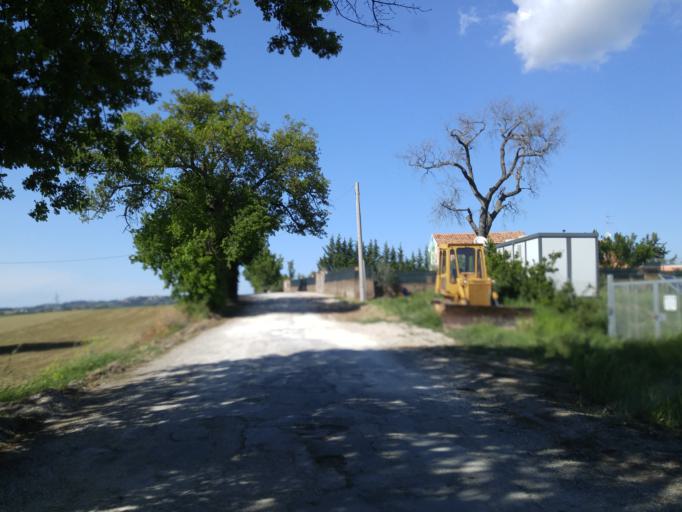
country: IT
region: The Marches
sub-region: Provincia di Pesaro e Urbino
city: Mombaroccio
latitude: 43.8073
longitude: 12.8880
